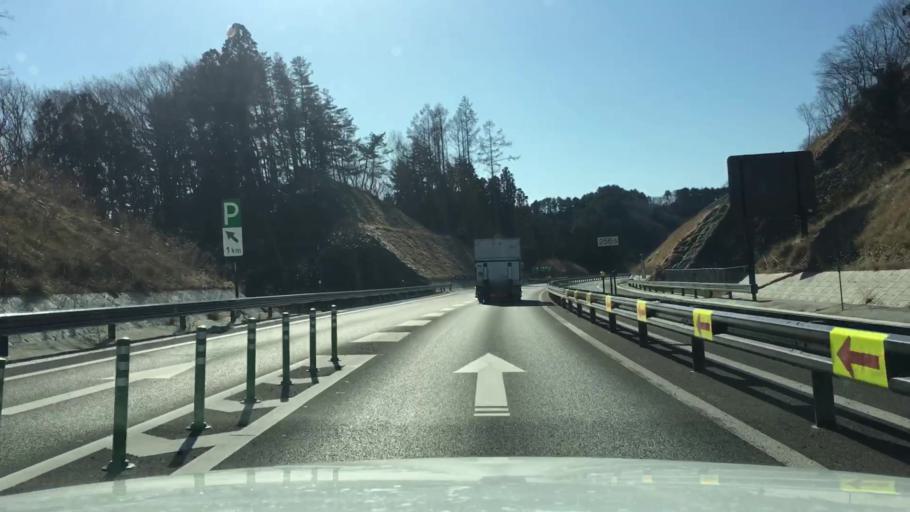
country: JP
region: Iwate
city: Miyako
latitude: 39.5937
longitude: 141.9405
